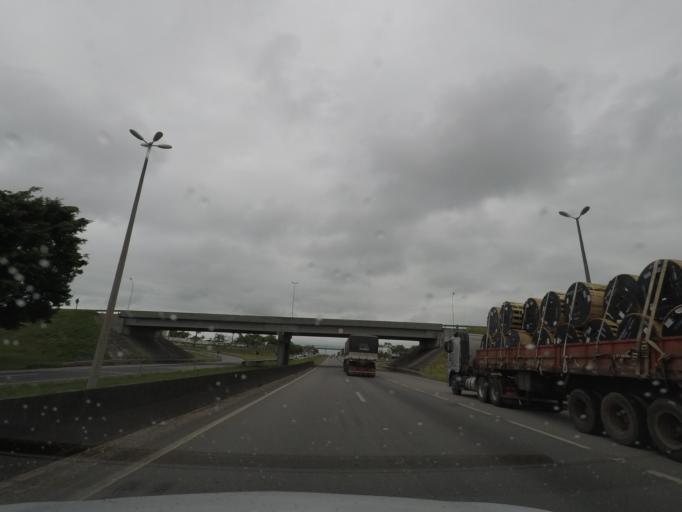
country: BR
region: Sao Paulo
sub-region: Registro
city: Registro
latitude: -24.4574
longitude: -47.8145
